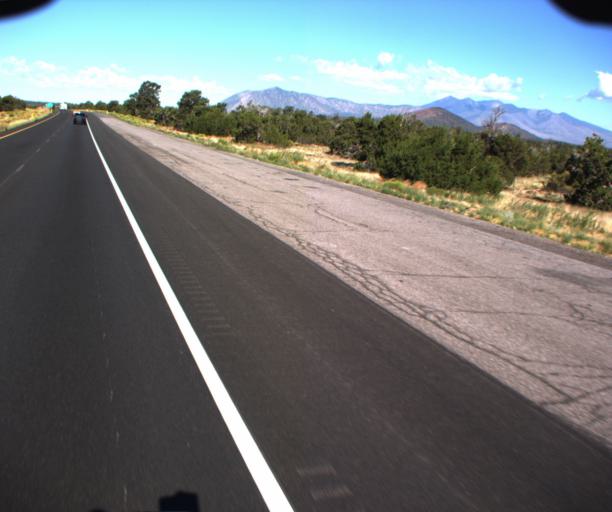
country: US
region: Arizona
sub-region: Coconino County
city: Flagstaff
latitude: 35.2028
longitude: -111.4635
